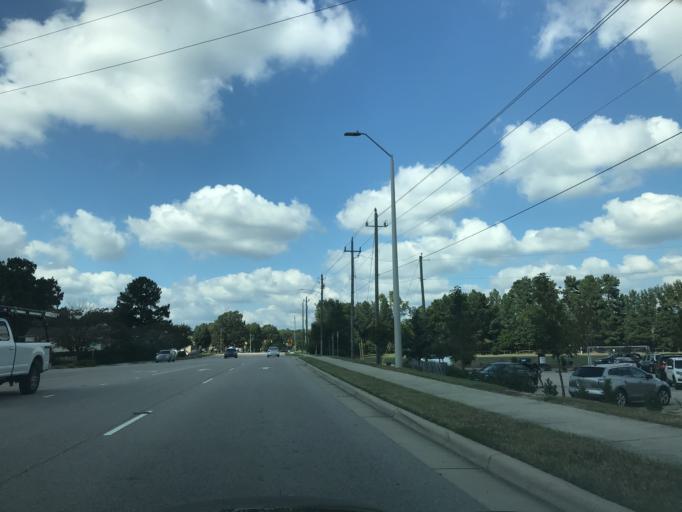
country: US
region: North Carolina
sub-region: Wake County
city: Rolesville
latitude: 35.8840
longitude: -78.5518
